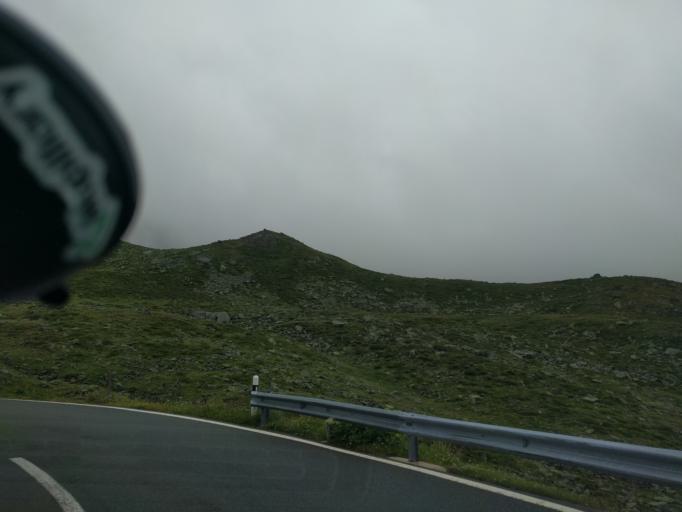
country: CH
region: Grisons
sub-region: Praettigau/Davos District
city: Davos
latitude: 46.7663
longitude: 9.9399
